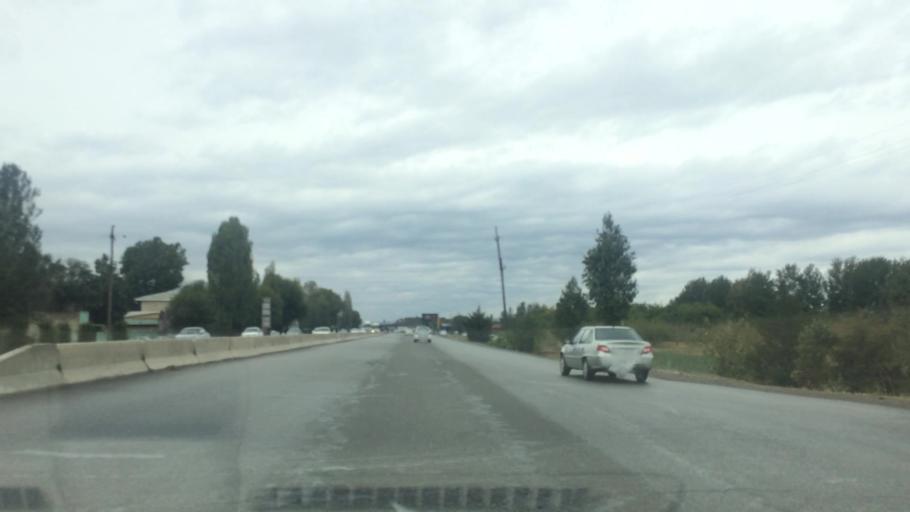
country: UZ
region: Jizzax
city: Jizzax
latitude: 40.0137
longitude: 67.6037
